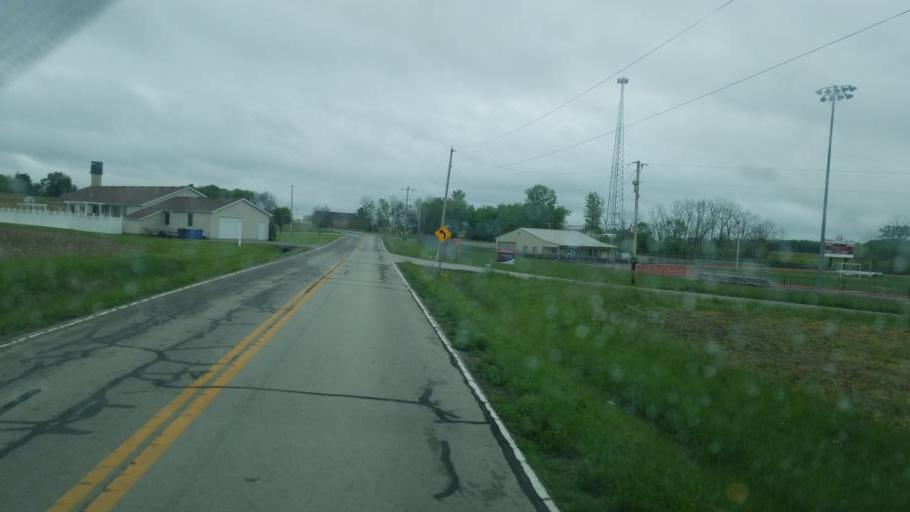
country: US
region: Ohio
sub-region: Highland County
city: Leesburg
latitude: 39.3300
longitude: -83.5517
